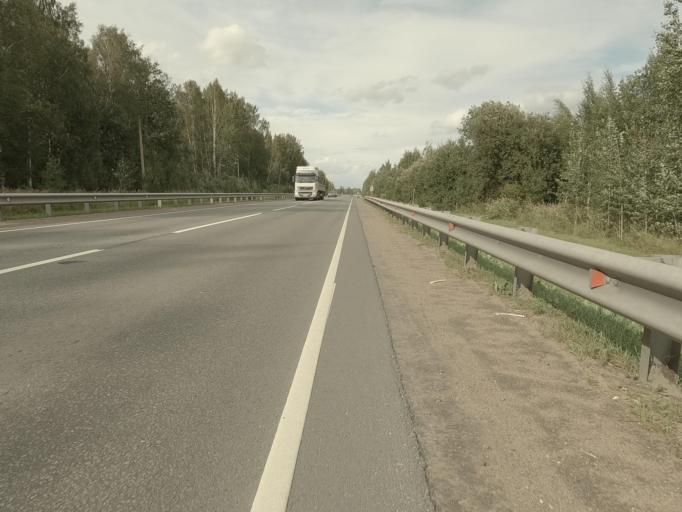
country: RU
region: Leningrad
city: Mga
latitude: 59.7881
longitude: 31.1072
